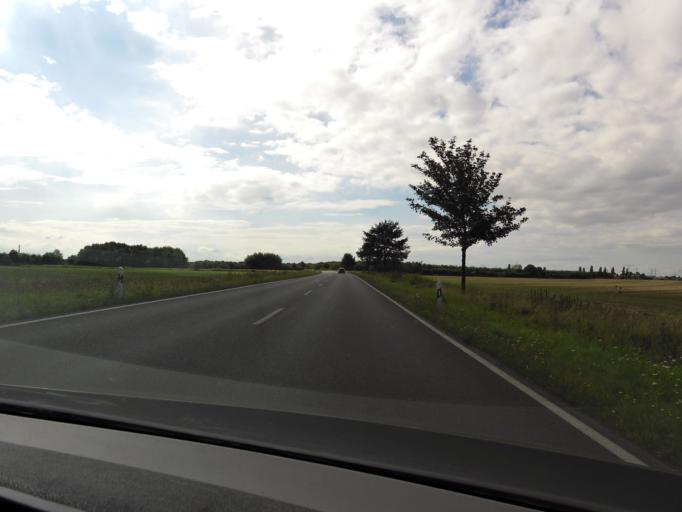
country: DE
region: Saxony
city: Borsdorf
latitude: 51.3552
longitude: 12.5083
